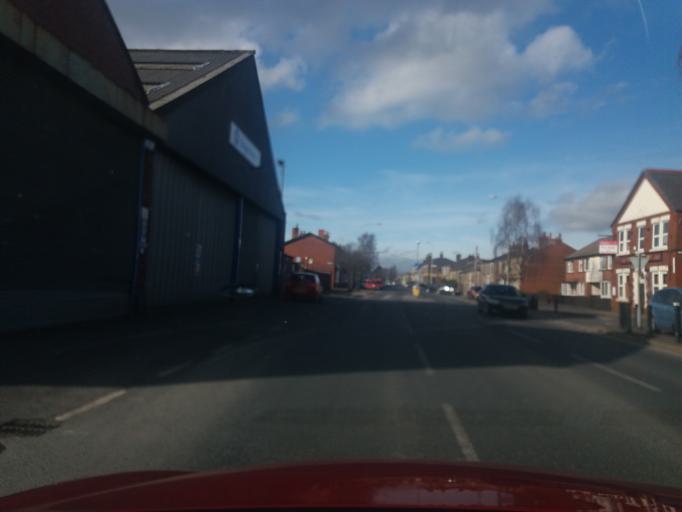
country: GB
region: England
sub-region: Lancashire
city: Chorley
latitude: 53.6508
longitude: -2.6175
